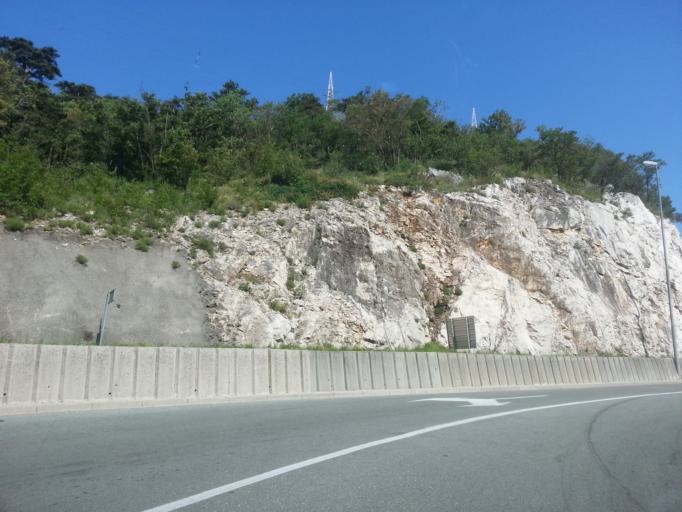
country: HR
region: Primorsko-Goranska
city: Bakar
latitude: 45.3041
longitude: 14.5271
